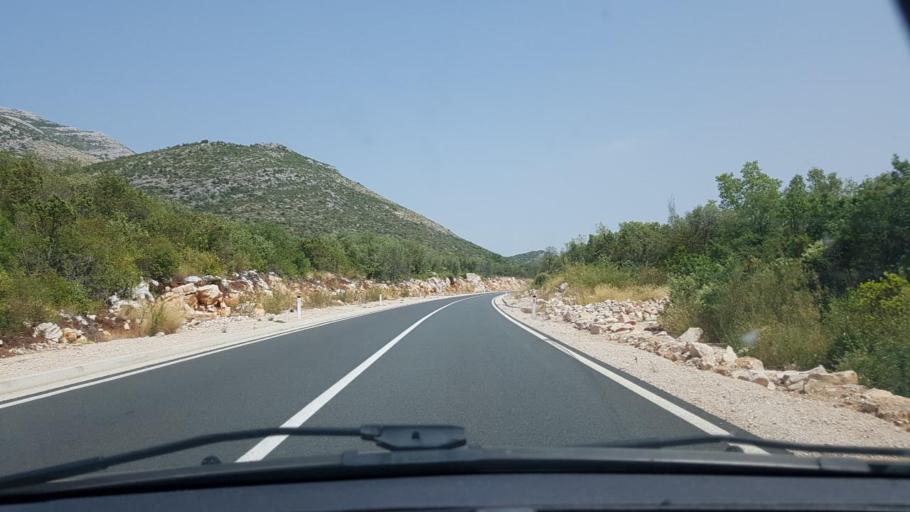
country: BA
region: Federation of Bosnia and Herzegovina
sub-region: Hercegovacko-Bosanski Kanton
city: Neum
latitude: 42.9589
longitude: 17.7186
